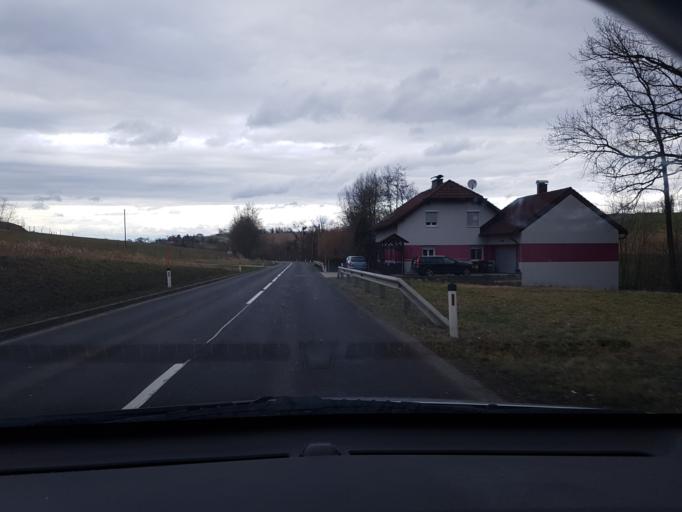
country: AT
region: Upper Austria
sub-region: Politischer Bezirk Linz-Land
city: Ansfelden
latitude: 48.1774
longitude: 14.2747
